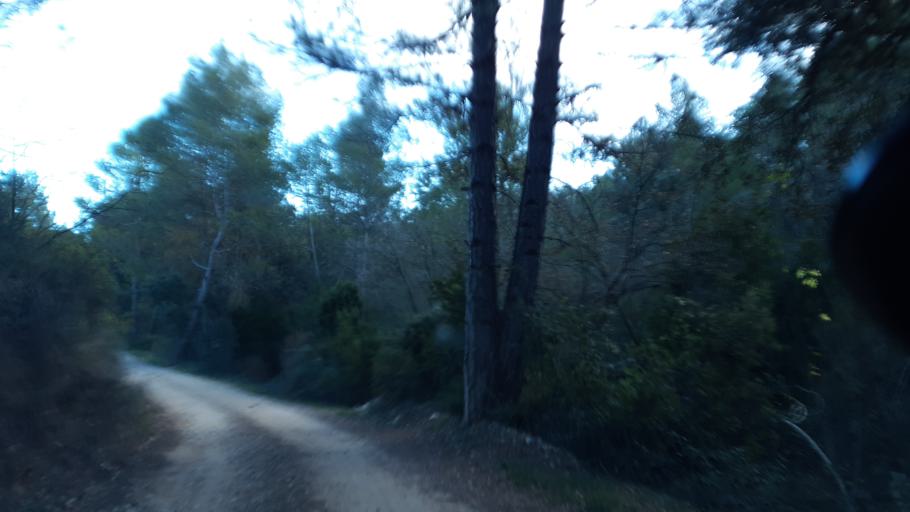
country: ES
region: Aragon
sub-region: Provincia de Teruel
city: Valderrobres
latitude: 40.8498
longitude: 0.2175
